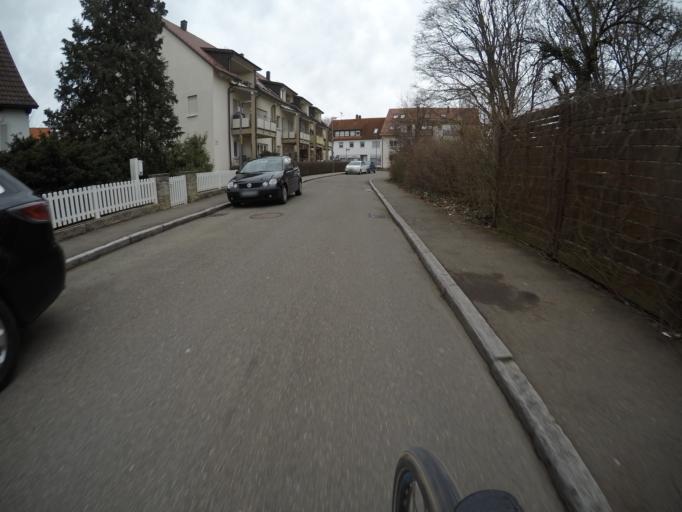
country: DE
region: Baden-Wuerttemberg
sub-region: Regierungsbezirk Stuttgart
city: Boeblingen
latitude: 48.6807
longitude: 9.0237
